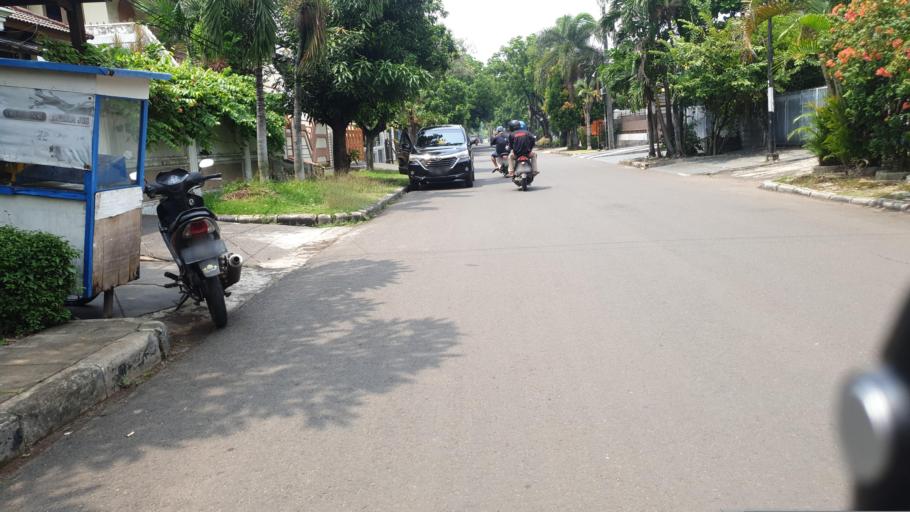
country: ID
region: West Java
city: Ciputat
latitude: -6.1950
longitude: 106.7491
